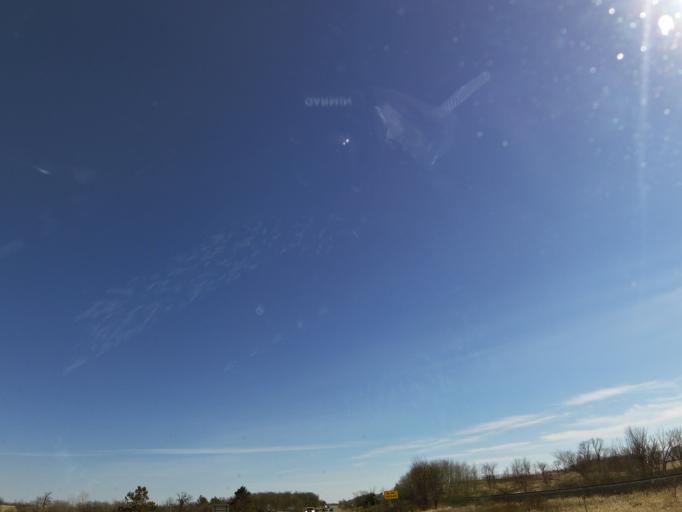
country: US
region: Minnesota
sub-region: Wright County
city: Buffalo
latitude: 45.1505
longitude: -93.8438
